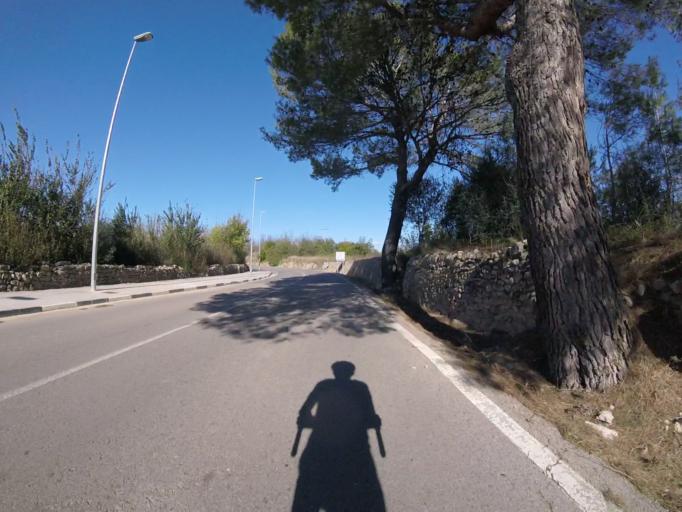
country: ES
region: Valencia
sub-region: Provincia de Castello
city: Chert/Xert
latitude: 40.4668
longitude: 0.1846
